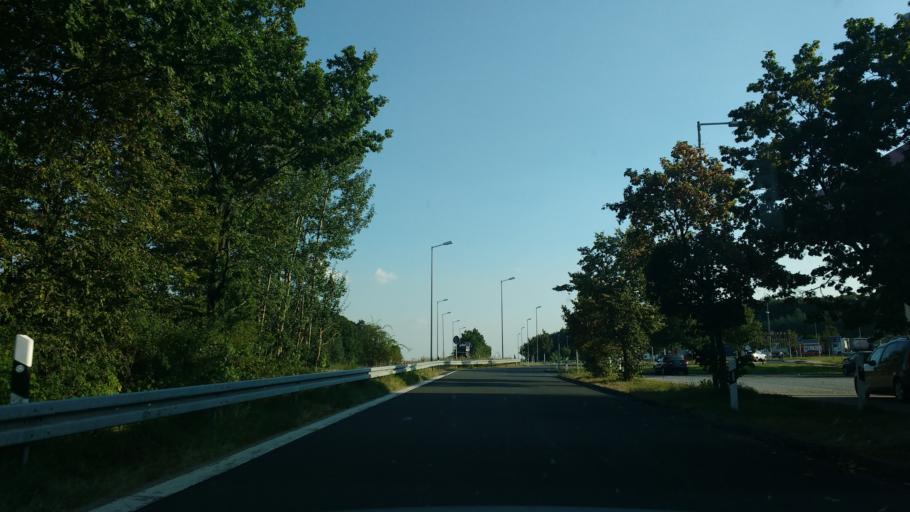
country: DE
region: Bavaria
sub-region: Regierungsbezirk Unterfranken
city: Schondra
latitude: 50.2651
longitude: 9.8813
